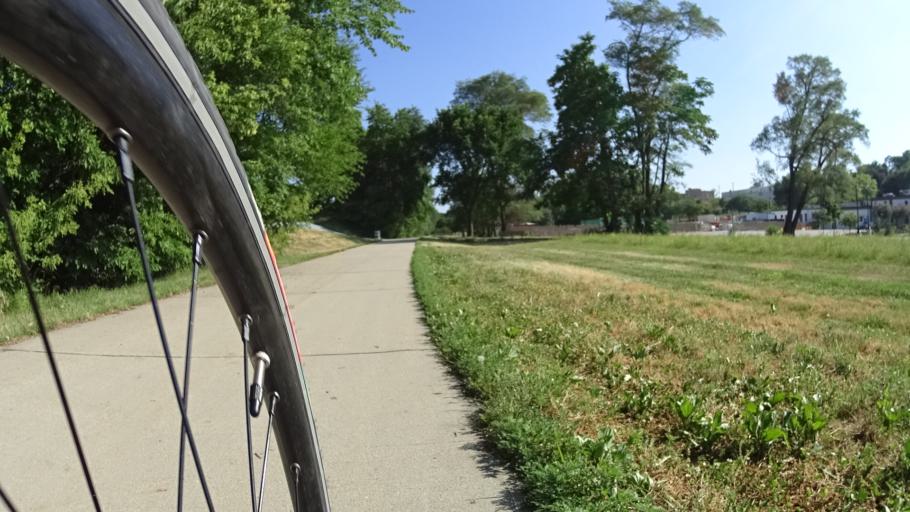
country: US
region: Nebraska
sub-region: Douglas County
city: Omaha
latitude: 41.2505
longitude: -95.9716
